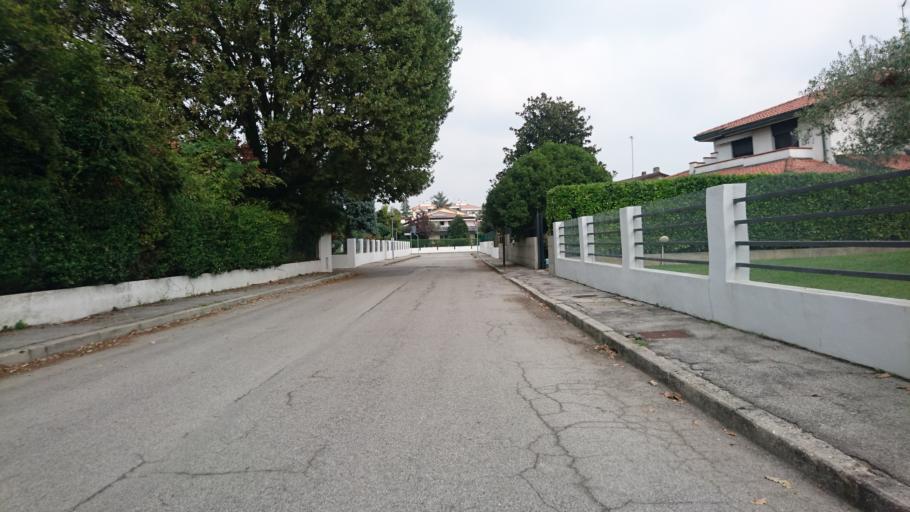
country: IT
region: Veneto
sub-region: Provincia di Padova
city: Tencarola
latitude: 45.3961
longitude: 11.8095
